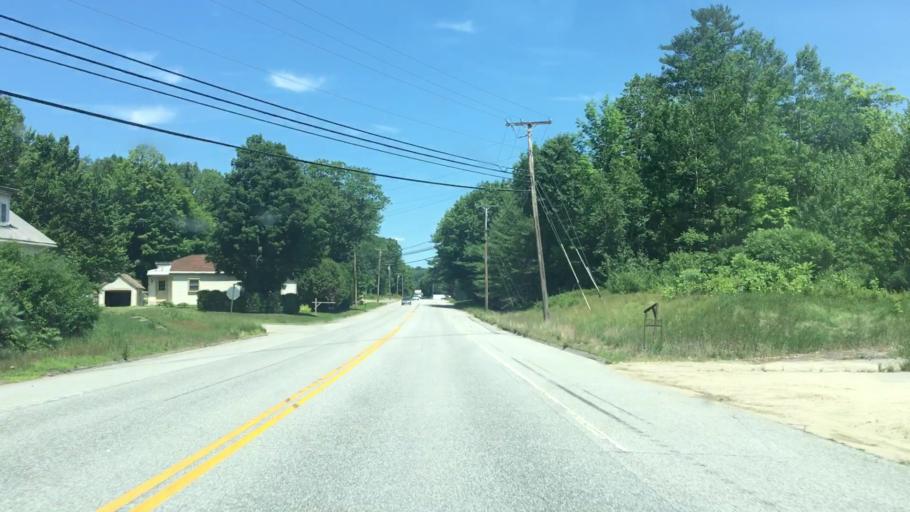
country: US
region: Maine
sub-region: Androscoggin County
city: Livermore Falls
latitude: 44.4629
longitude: -70.1932
